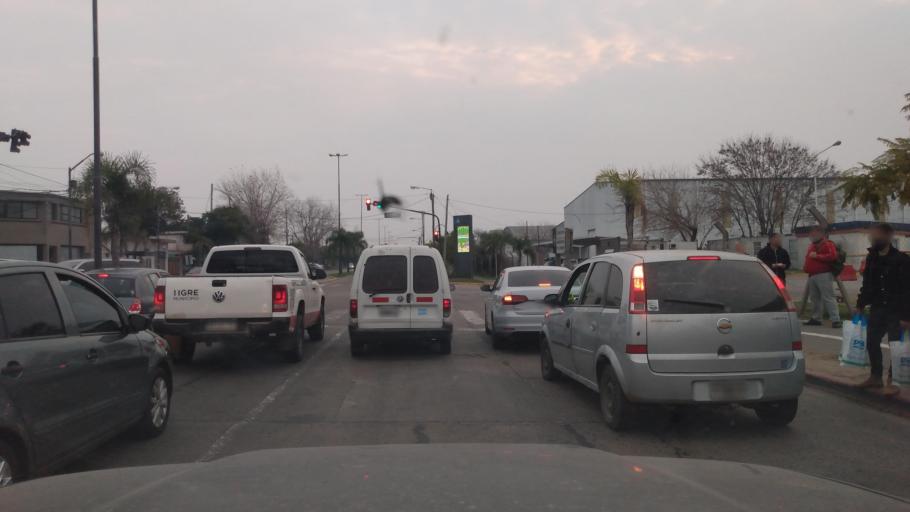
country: AR
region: Buenos Aires
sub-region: Partido de Tigre
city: Tigre
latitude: -34.4564
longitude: -58.5838
